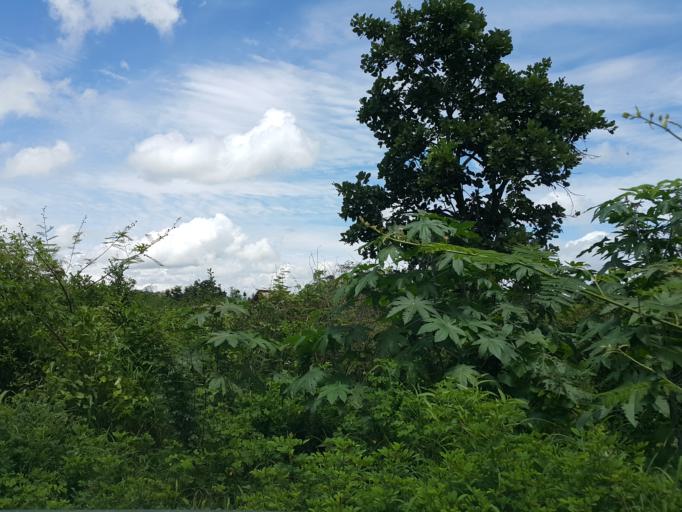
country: TH
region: Chiang Mai
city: San Kamphaeng
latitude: 18.7594
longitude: 99.1071
